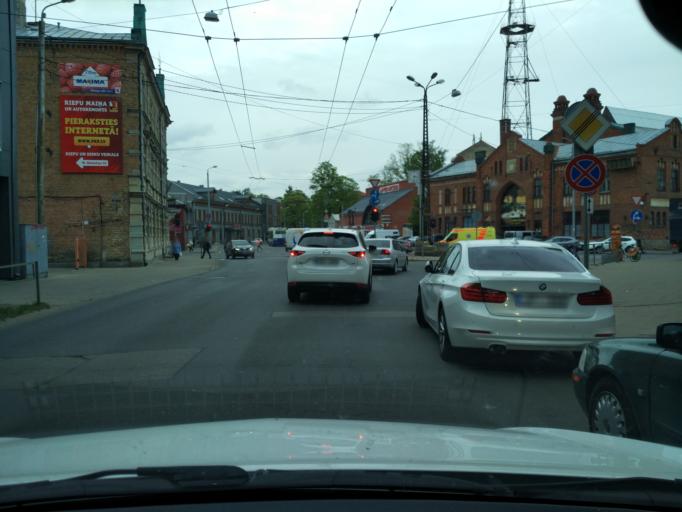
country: LV
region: Marupe
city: Marupe
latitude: 56.9350
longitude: 24.0711
